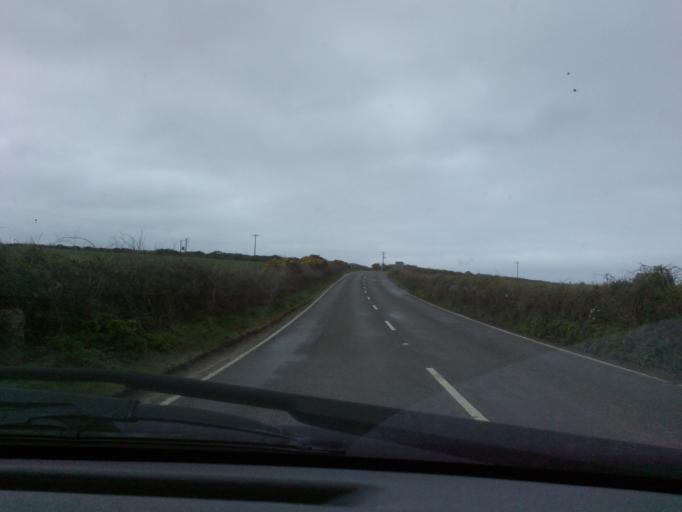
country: GB
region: England
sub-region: Cornwall
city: Saint Just
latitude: 50.1208
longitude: -5.6665
